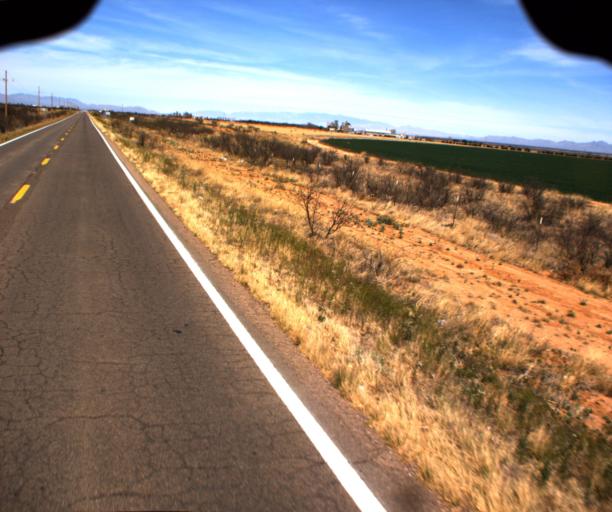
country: US
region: Arizona
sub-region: Cochise County
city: Willcox
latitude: 31.9725
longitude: -109.8471
